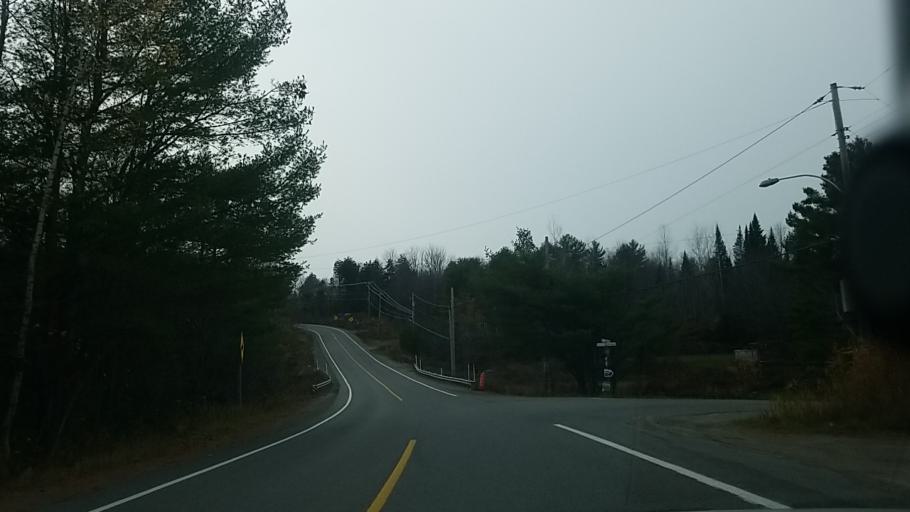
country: CA
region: Quebec
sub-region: Laurentides
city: Saint-Colomban
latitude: 45.7905
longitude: -74.1318
